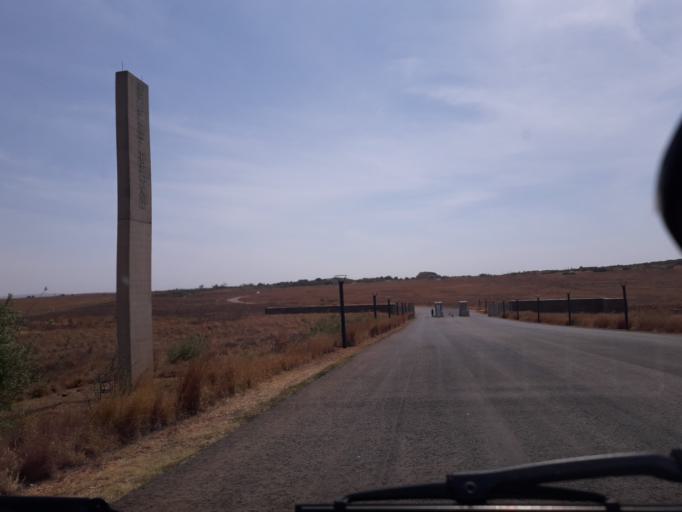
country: ZA
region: Gauteng
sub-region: West Rand District Municipality
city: Krugersdorp
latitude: -25.9784
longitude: 27.6643
